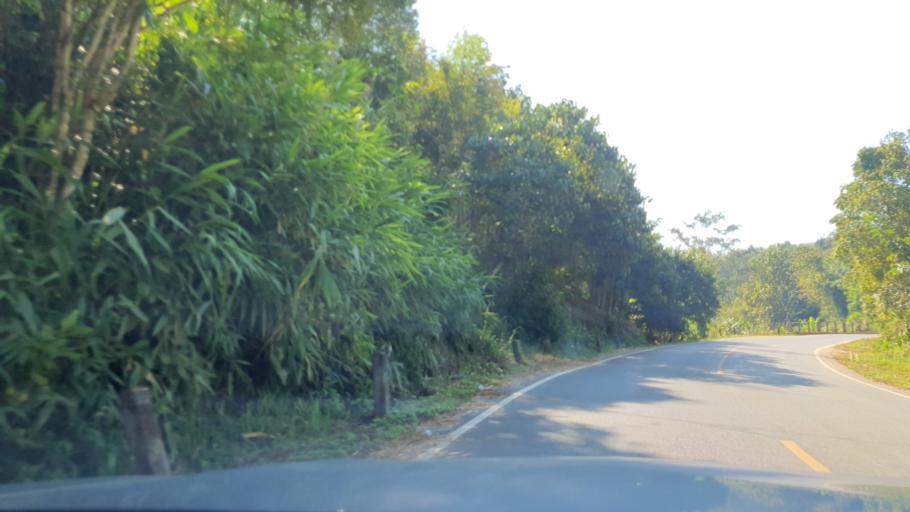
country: TH
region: Nan
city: Pua
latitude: 19.1623
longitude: 100.9077
